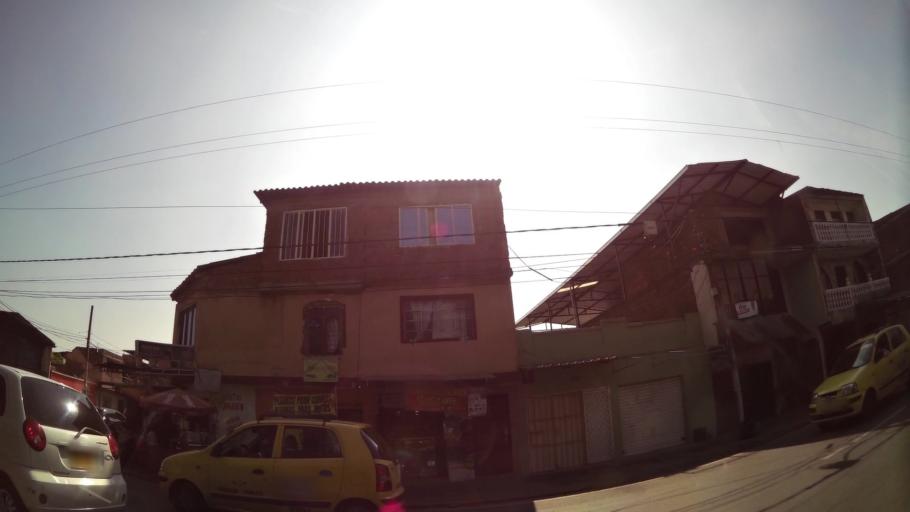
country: CO
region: Valle del Cauca
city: Cali
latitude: 3.4185
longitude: -76.5211
